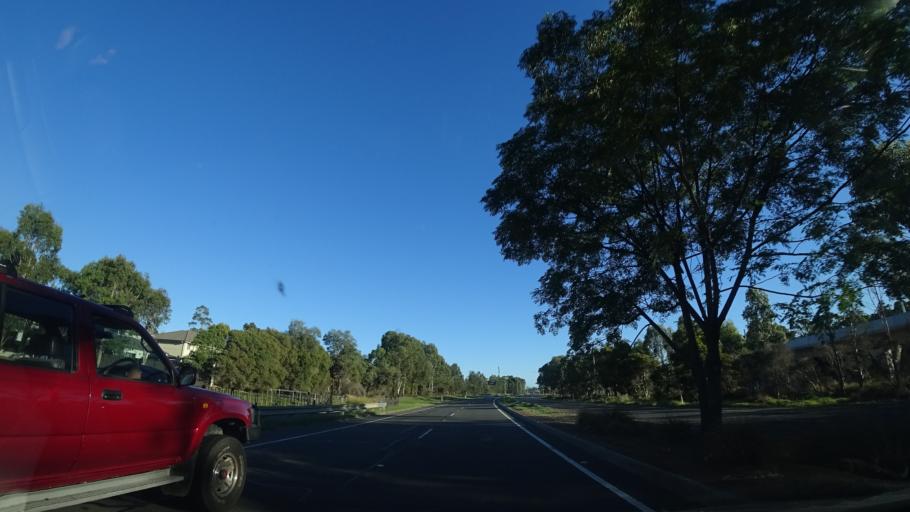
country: AU
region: New South Wales
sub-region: Blacktown
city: Stanhope Gardens
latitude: -33.7085
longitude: 150.9316
